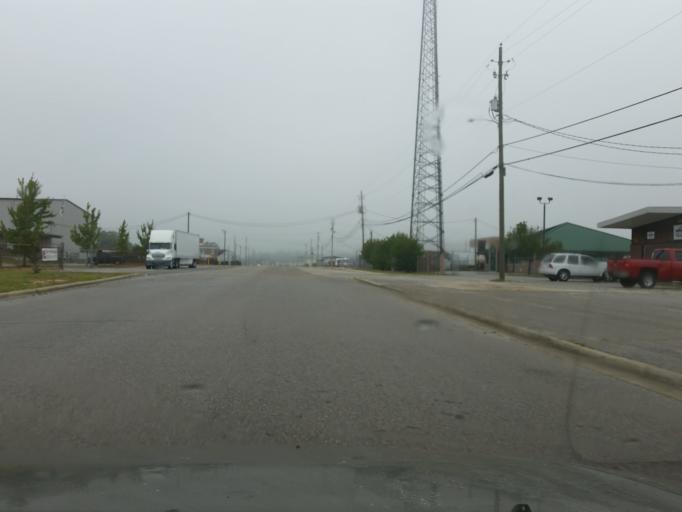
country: US
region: Florida
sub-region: Escambia County
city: Ferry Pass
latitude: 30.5239
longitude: -87.1977
